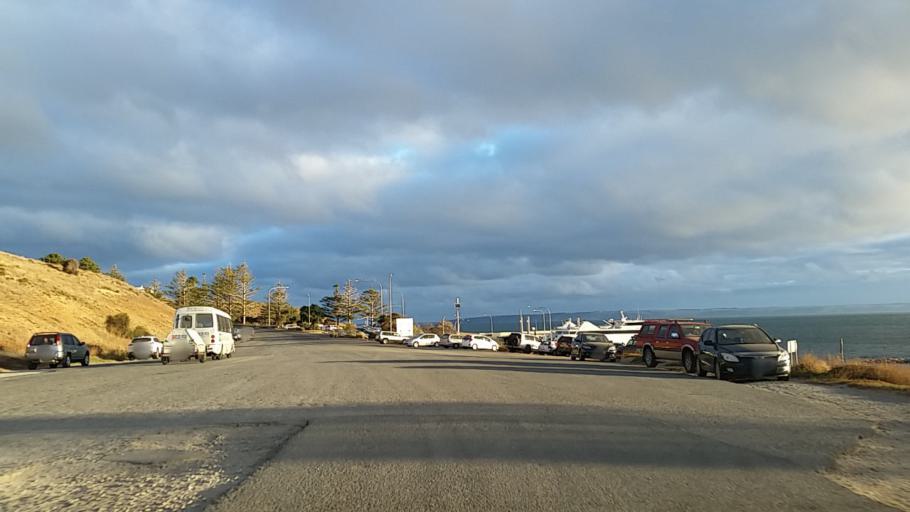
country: AU
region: South Australia
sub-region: Yankalilla
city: Normanville
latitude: -35.6040
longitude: 138.0951
